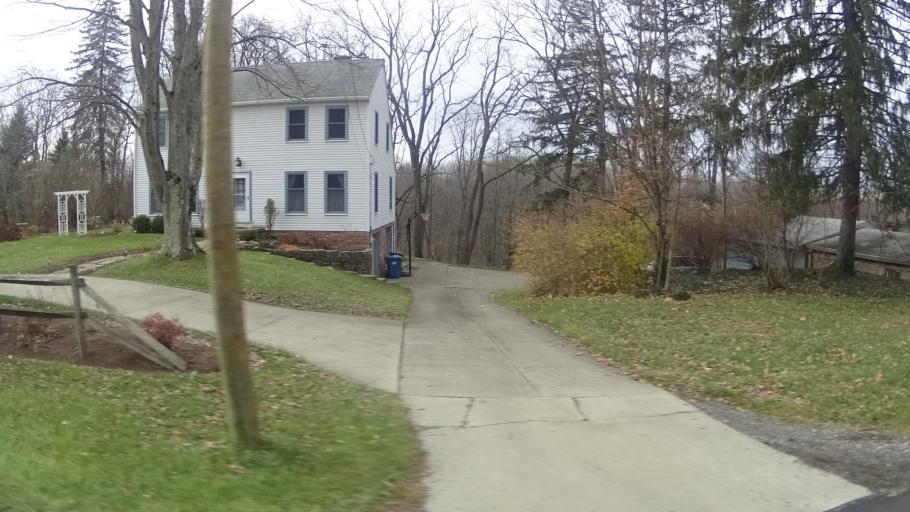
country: US
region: Ohio
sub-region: Cuyahoga County
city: Strongsville
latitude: 41.2916
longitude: -81.9115
